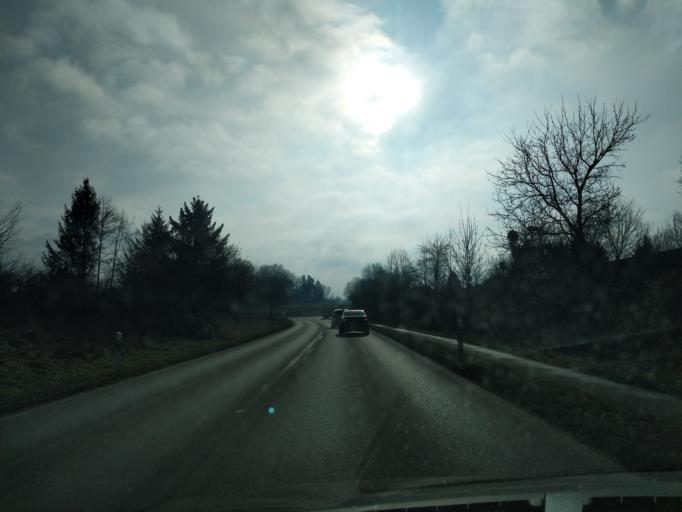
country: DE
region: Baden-Wuerttemberg
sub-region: Tuebingen Region
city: Markdorf
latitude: 47.7060
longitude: 9.4004
